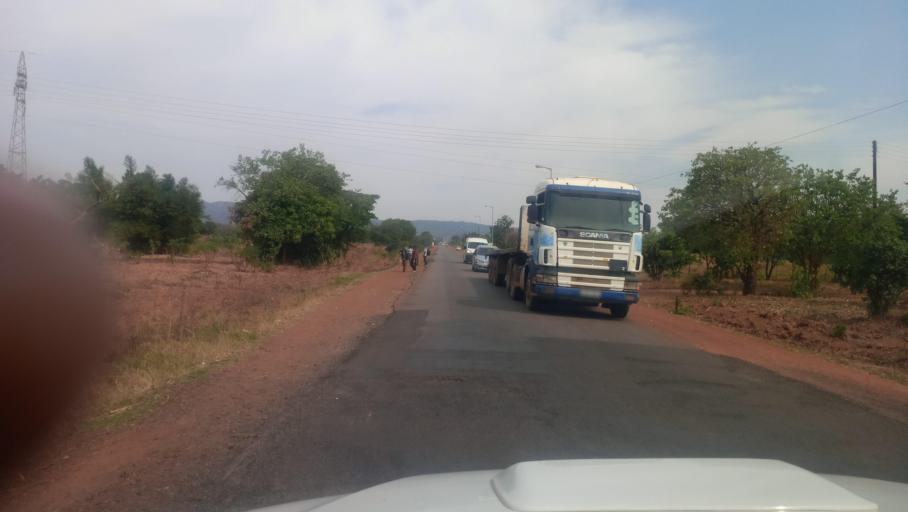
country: ZM
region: Northern
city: Mpika
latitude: -11.8352
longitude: 31.4275
